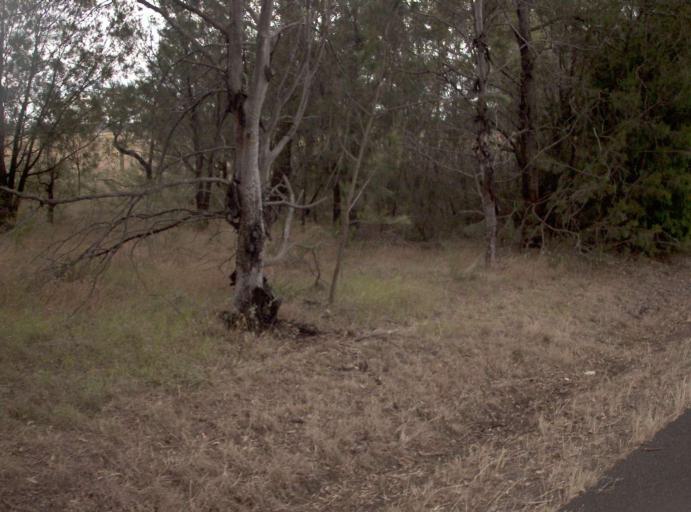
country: AU
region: Victoria
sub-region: Wellington
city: Sale
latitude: -38.3630
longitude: 146.9911
